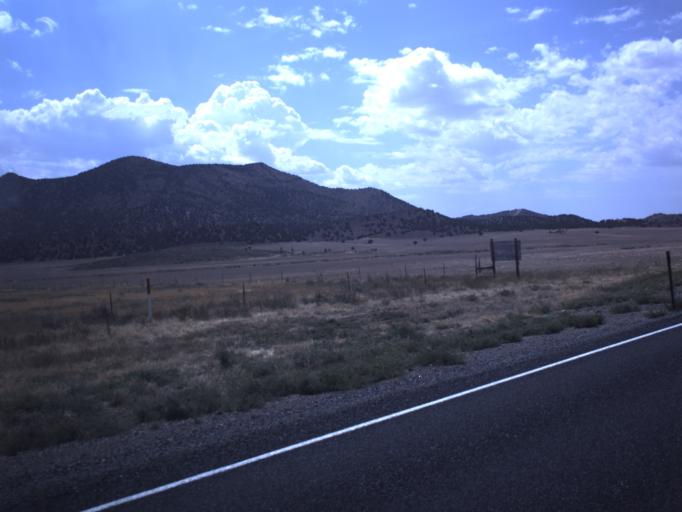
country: US
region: Utah
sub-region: Utah County
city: Eagle Mountain
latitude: 40.2429
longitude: -112.1437
